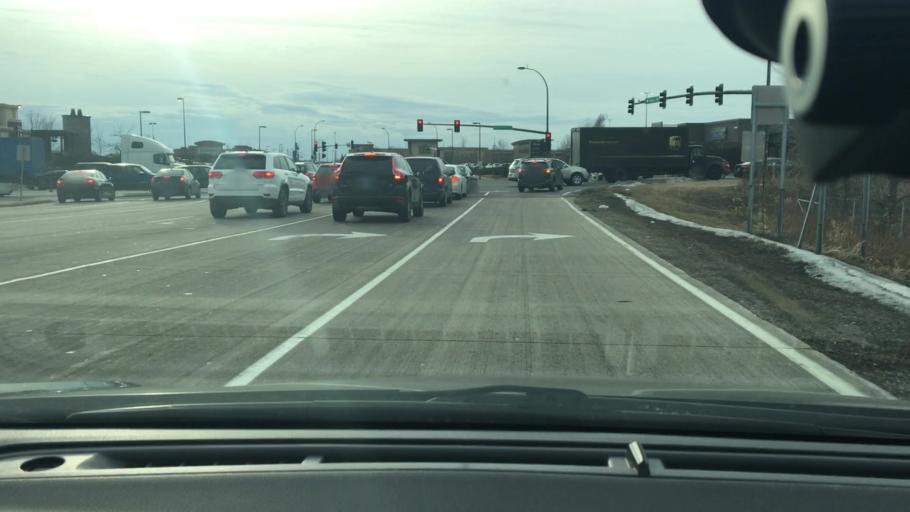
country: US
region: Minnesota
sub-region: Hennepin County
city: Maple Grove
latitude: 45.0912
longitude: -93.4307
